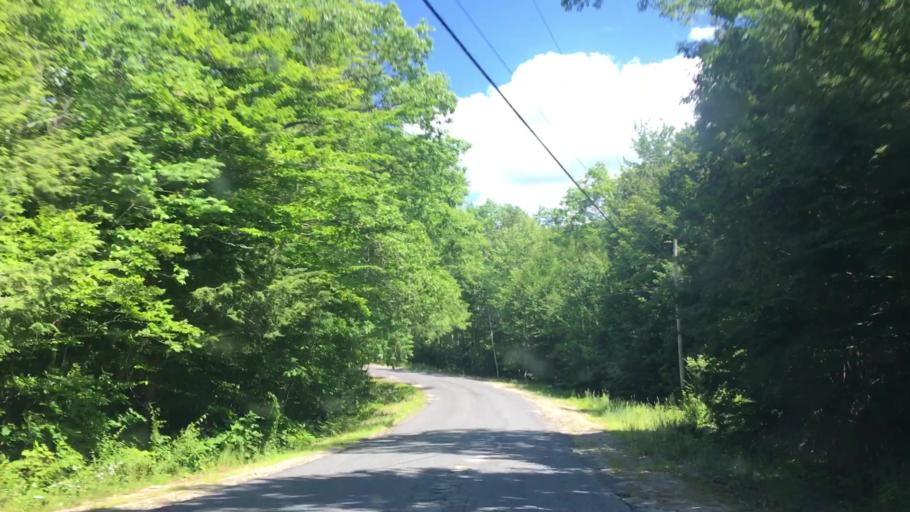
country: US
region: Maine
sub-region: Franklin County
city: Chesterville
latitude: 44.5586
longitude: -70.1246
